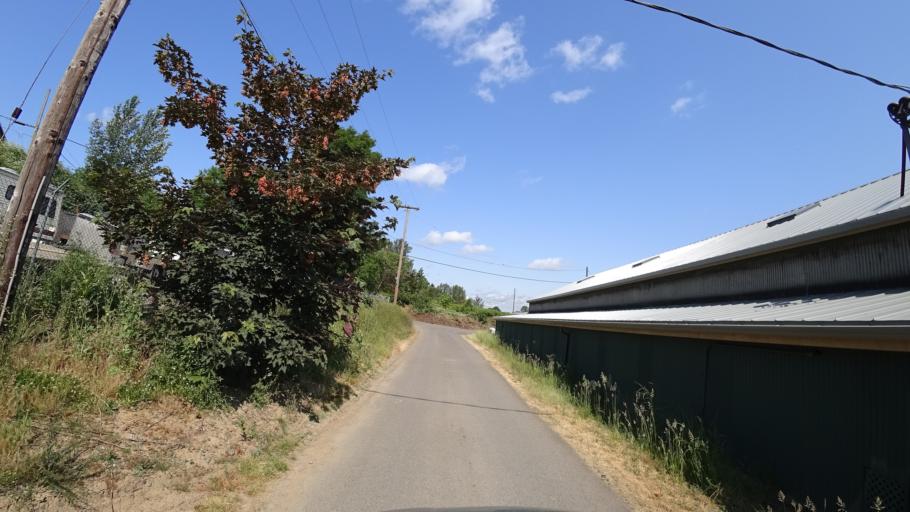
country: US
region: Washington
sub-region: Clark County
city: Vancouver
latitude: 45.5989
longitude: -122.7319
